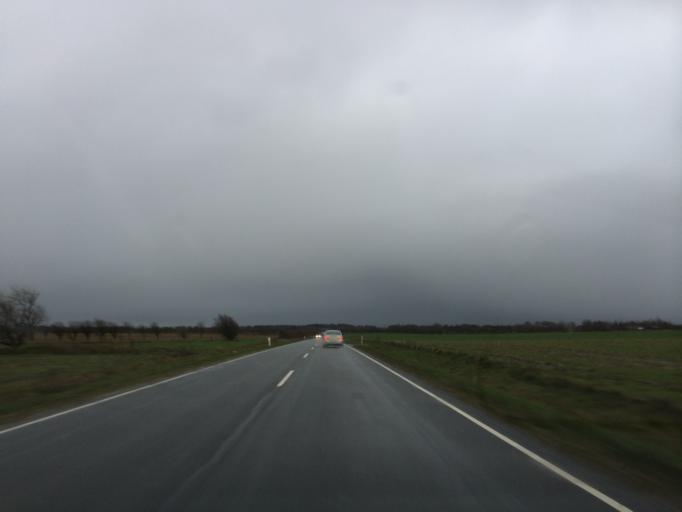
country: DK
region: South Denmark
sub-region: Varde Kommune
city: Varde
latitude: 55.7163
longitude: 8.4942
